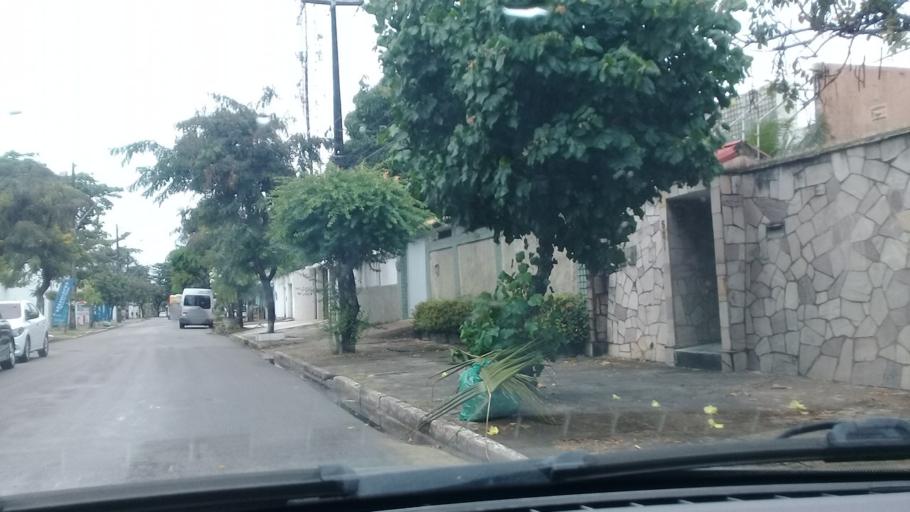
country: BR
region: Pernambuco
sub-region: Recife
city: Recife
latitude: -8.1393
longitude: -34.9146
